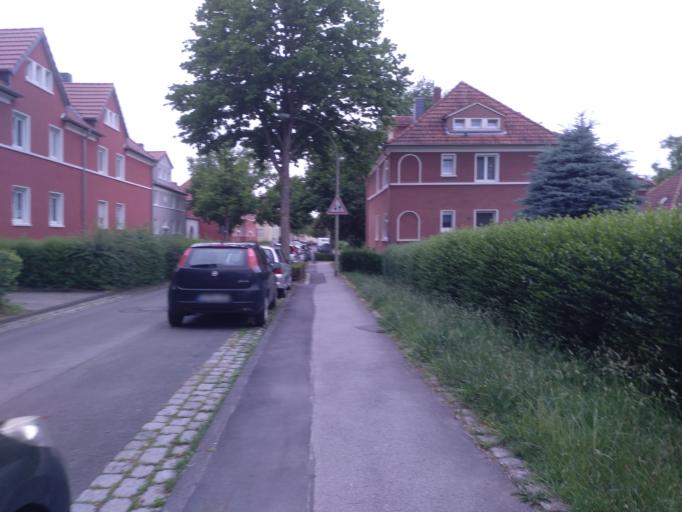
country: DE
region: North Rhine-Westphalia
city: Witten
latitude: 51.4378
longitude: 7.3594
